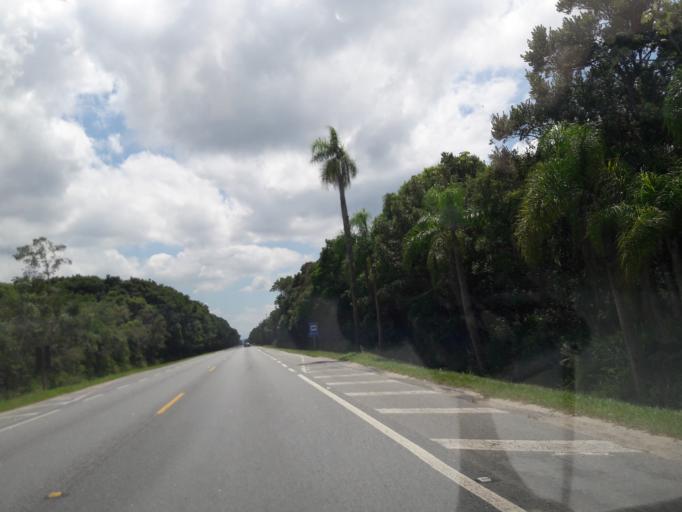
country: BR
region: Parana
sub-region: Pontal Do Parana
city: Pontal do Parana
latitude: -25.6269
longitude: -48.5416
